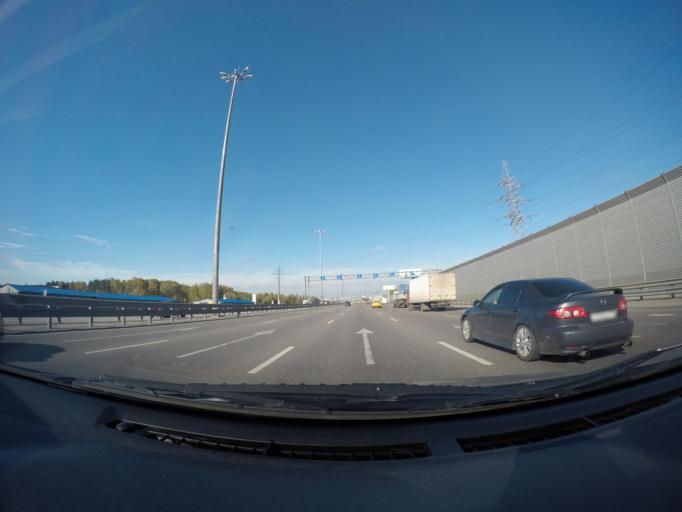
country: RU
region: Moskovskaya
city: Tomilino
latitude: 55.6379
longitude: 37.9250
